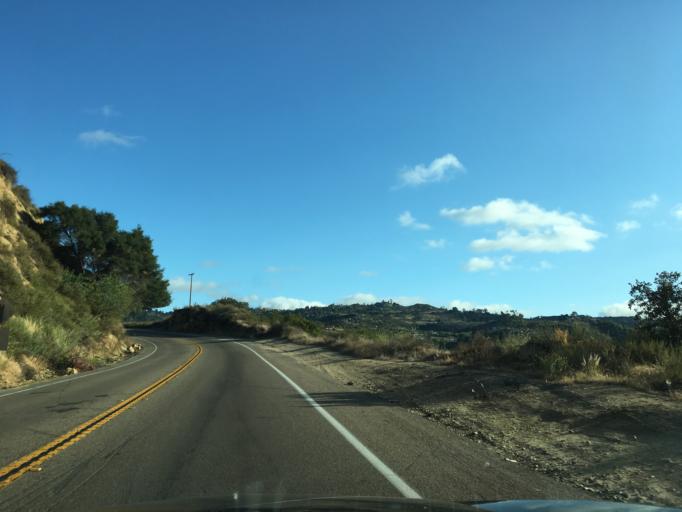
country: US
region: California
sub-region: San Diego County
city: Hidden Meadows
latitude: 33.2553
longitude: -117.1105
